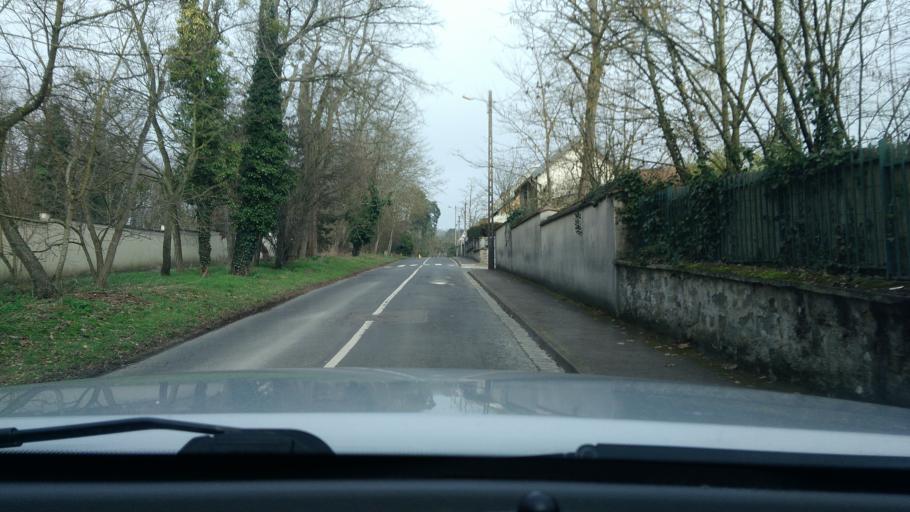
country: FR
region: Ile-de-France
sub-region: Departement de Seine-et-Marne
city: Fontainebleau
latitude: 48.4137
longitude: 2.6977
